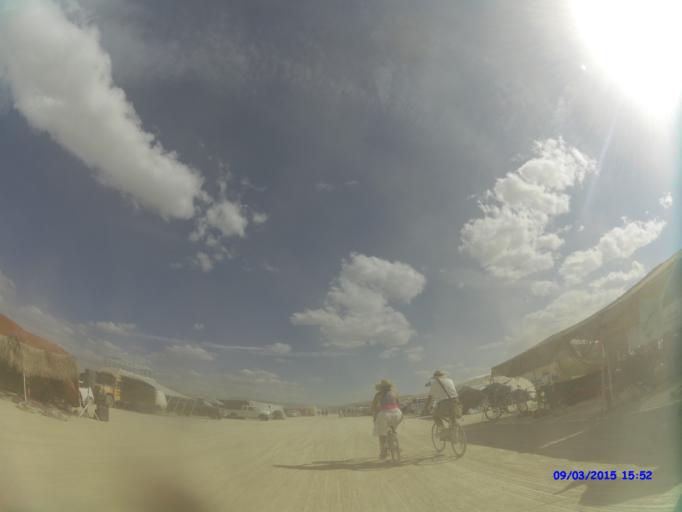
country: US
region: Nevada
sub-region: Pershing County
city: Lovelock
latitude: 40.7831
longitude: -119.2181
